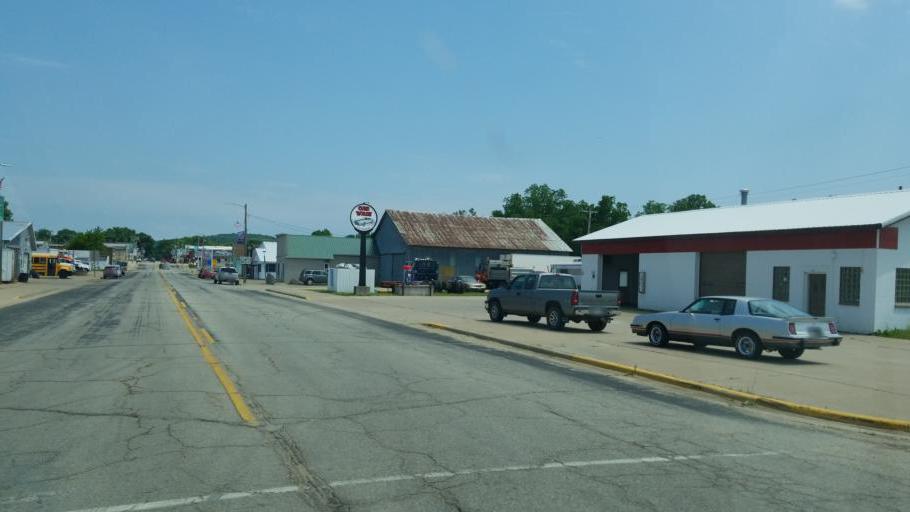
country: US
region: Wisconsin
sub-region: Monroe County
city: Cashton
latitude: 43.5744
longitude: -90.6413
